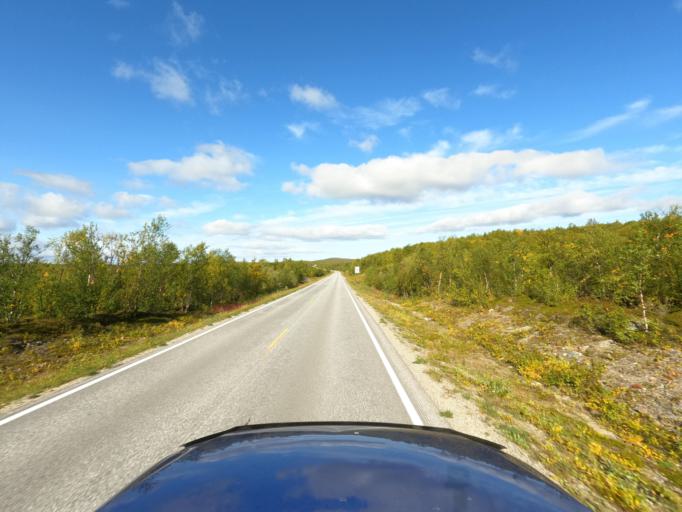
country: NO
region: Finnmark Fylke
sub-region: Karasjok
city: Karasjohka
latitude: 69.5371
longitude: 25.4322
